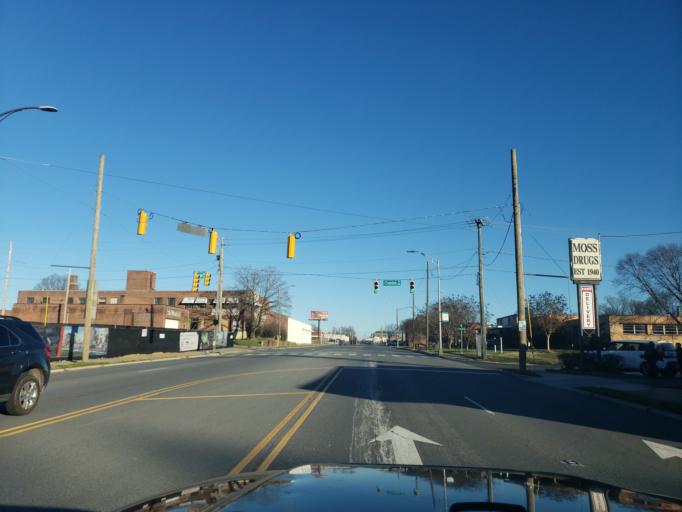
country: US
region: North Carolina
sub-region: Gaston County
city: Gastonia
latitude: 35.2623
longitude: -81.1937
